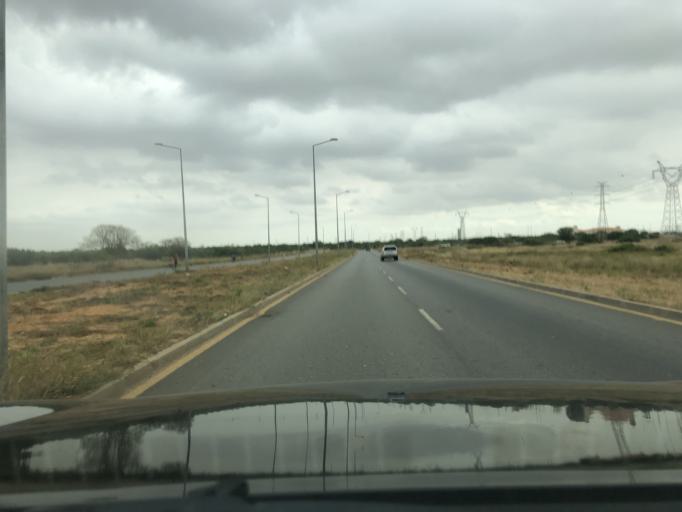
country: AO
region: Luanda
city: Luanda
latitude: -8.9757
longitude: 13.2797
